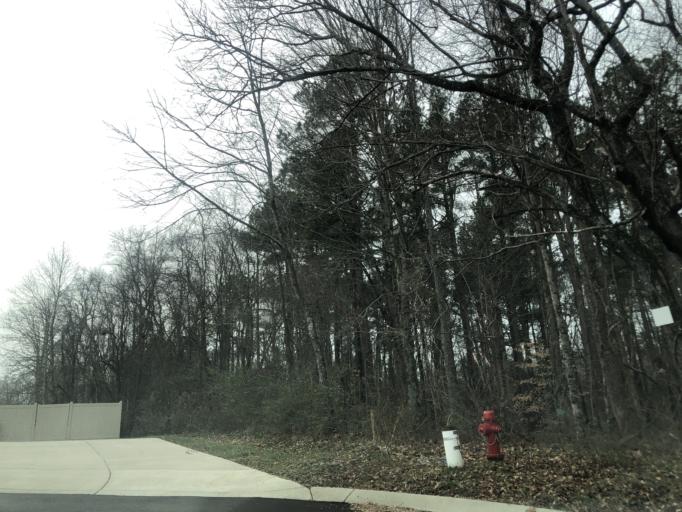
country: US
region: Tennessee
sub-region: Robertson County
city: Greenbrier
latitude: 36.4019
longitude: -86.8231
